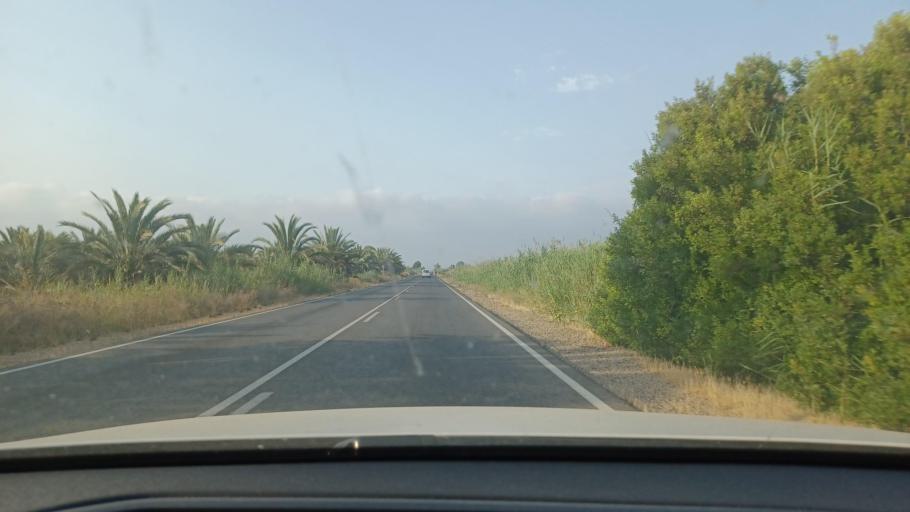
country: ES
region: Valencia
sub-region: Provincia de Alicante
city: Dolores
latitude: 38.1761
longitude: -0.7020
